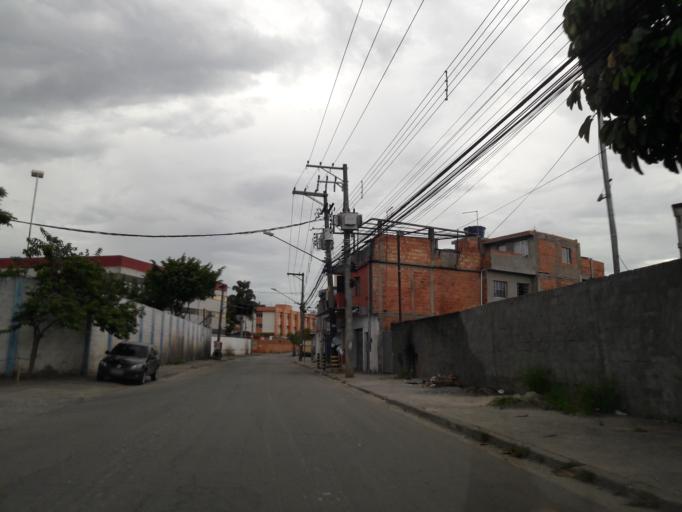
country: BR
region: Sao Paulo
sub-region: Aruja
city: Aruja
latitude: -23.4216
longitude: -46.3966
